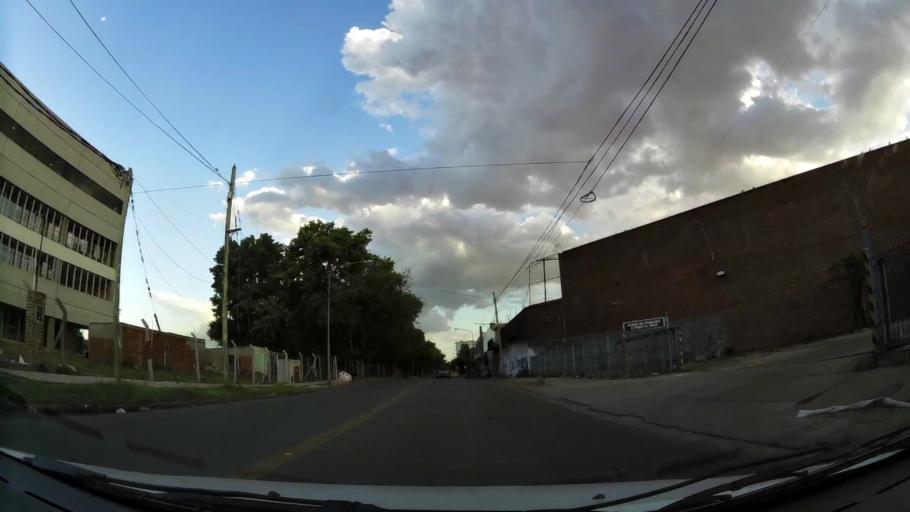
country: AR
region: Buenos Aires
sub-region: Partido de General San Martin
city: General San Martin
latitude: -34.5812
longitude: -58.5235
